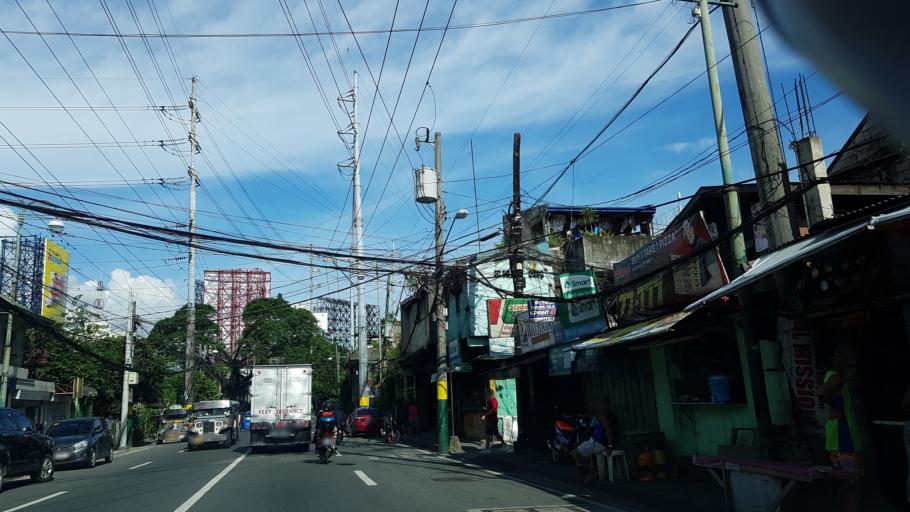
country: PH
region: Calabarzon
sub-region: Province of Rizal
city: Pateros
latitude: 14.5602
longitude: 121.0640
